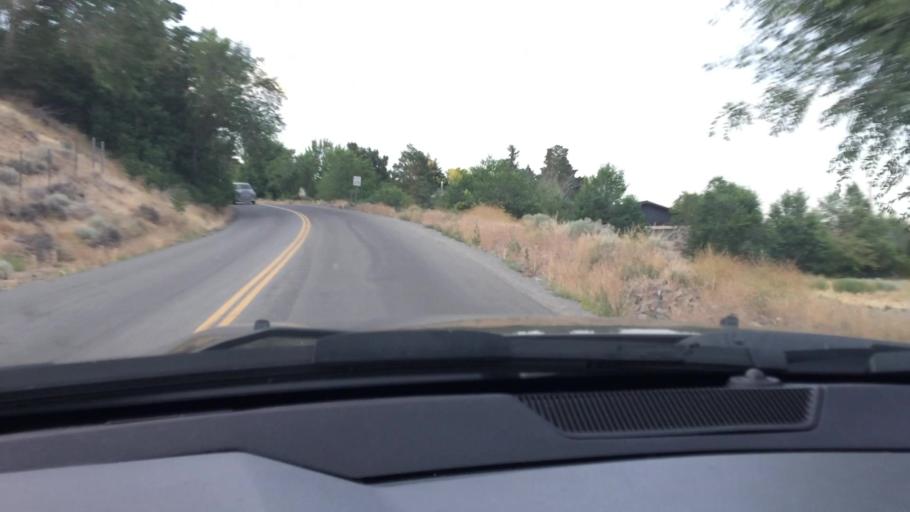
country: US
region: Nevada
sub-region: Washoe County
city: Reno
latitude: 39.4979
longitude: -119.8375
